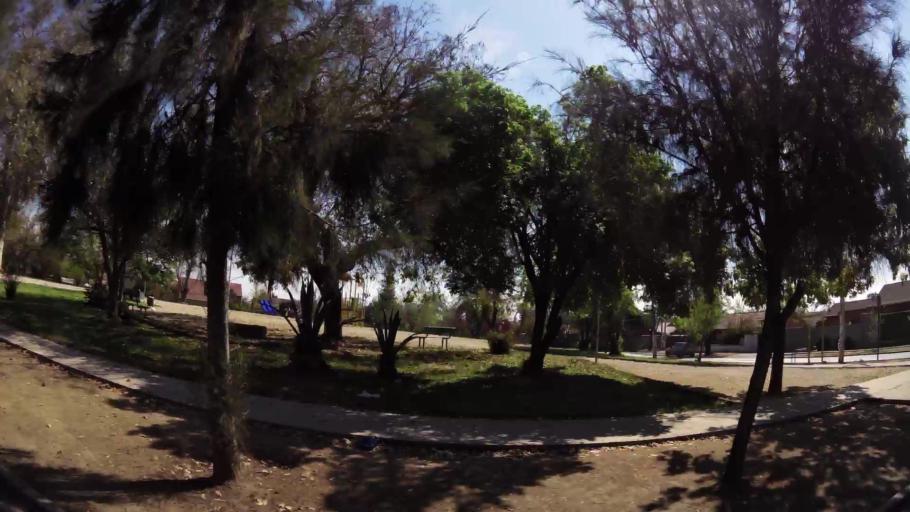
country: CL
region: Santiago Metropolitan
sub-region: Provincia de Santiago
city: Villa Presidente Frei, Nunoa, Santiago, Chile
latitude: -33.4900
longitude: -70.5872
